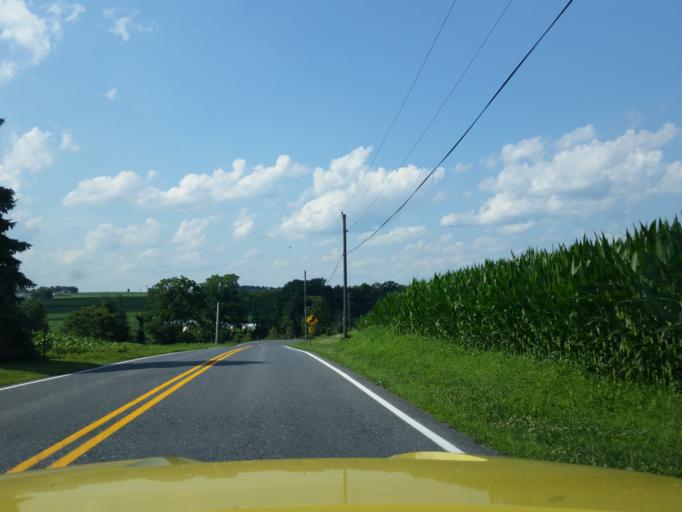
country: US
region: Pennsylvania
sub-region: Lancaster County
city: Salunga
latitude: 40.1416
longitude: -76.4527
